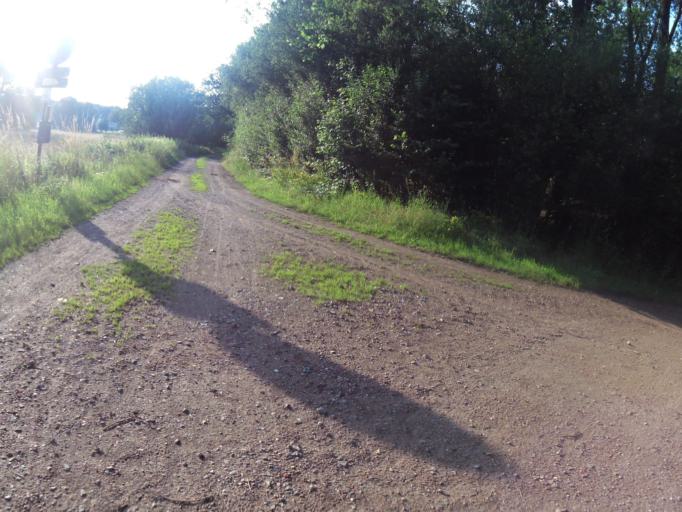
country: BE
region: Flanders
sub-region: Provincie Antwerpen
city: Herselt
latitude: 51.0016
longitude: 4.9049
